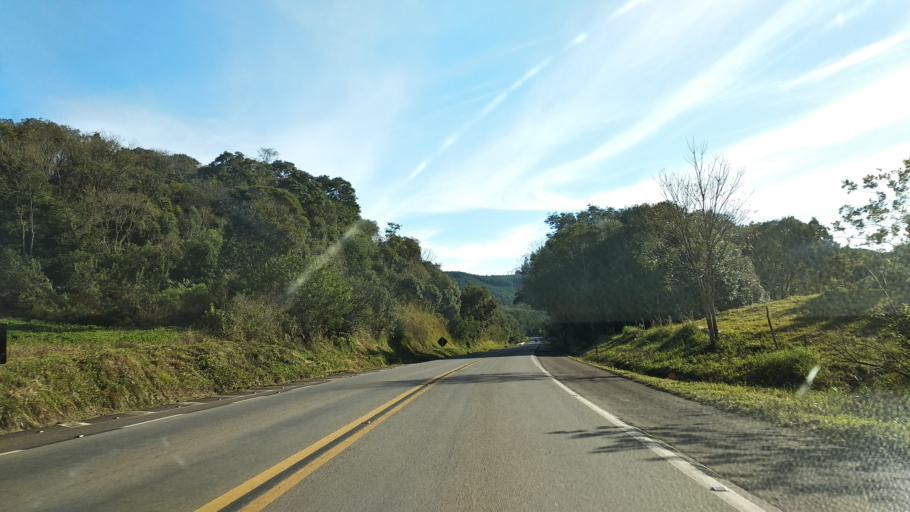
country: BR
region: Santa Catarina
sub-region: Celso Ramos
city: Celso Ramos
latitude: -27.5491
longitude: -51.4381
